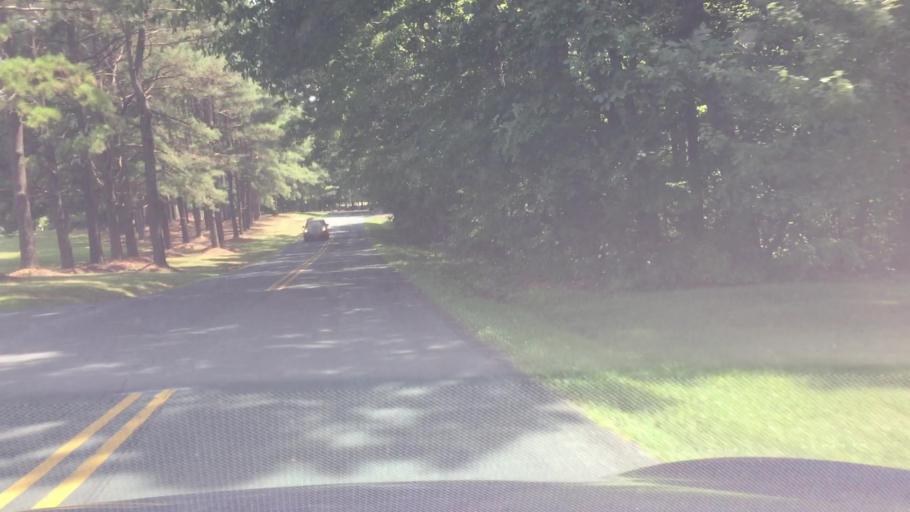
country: US
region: Virginia
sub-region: Appomattox County
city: Appomattox
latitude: 37.3323
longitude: -78.8783
